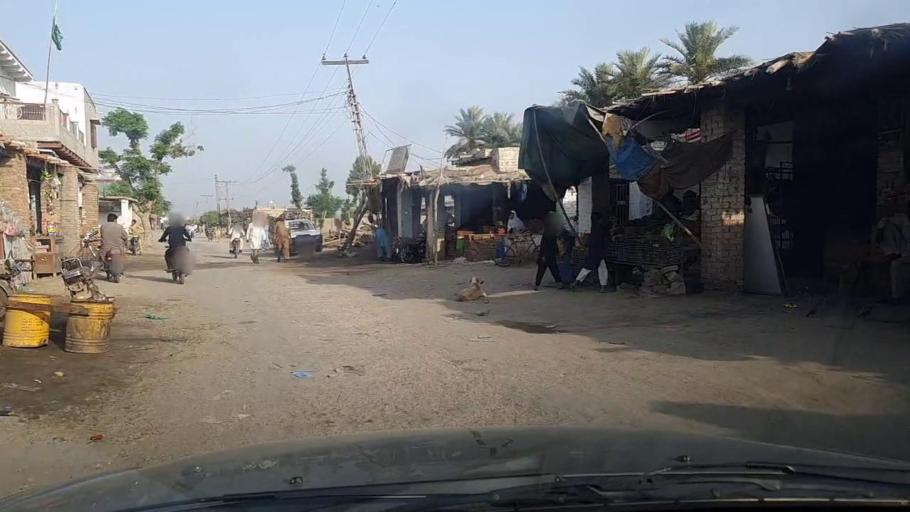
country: PK
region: Sindh
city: Pir jo Goth
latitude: 27.5580
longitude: 68.6745
